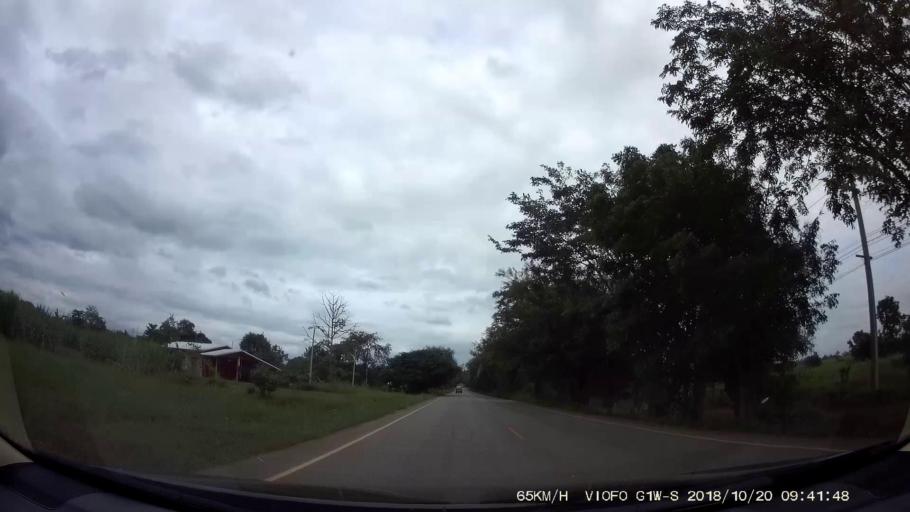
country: TH
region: Chaiyaphum
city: Khon San
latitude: 16.4569
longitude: 101.9554
